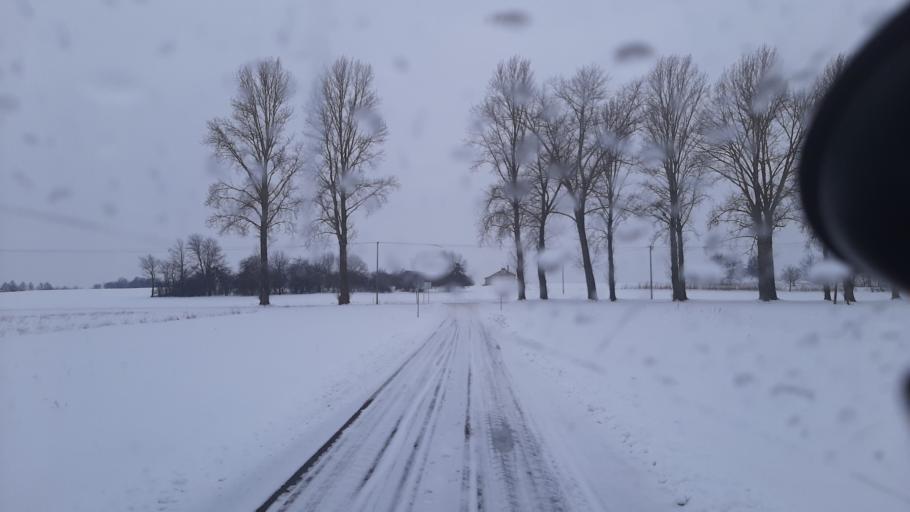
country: PL
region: Lublin Voivodeship
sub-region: Powiat lubelski
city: Jastkow
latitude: 51.3460
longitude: 22.3913
